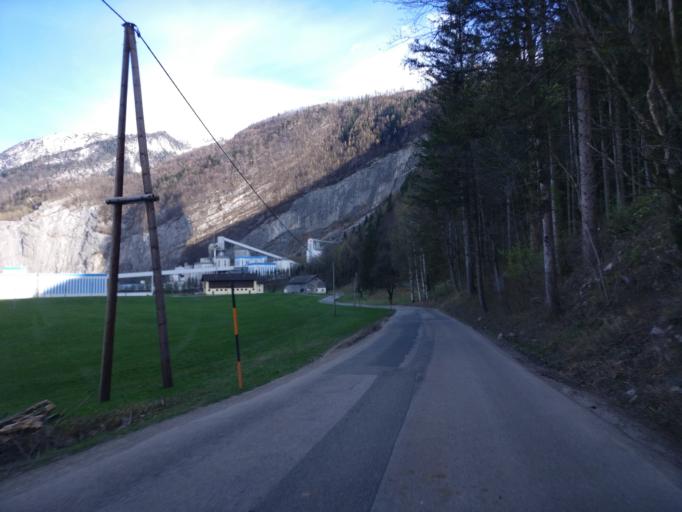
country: AT
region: Salzburg
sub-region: Politischer Bezirk Hallein
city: Golling an der Salzach
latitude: 47.5804
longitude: 13.1716
